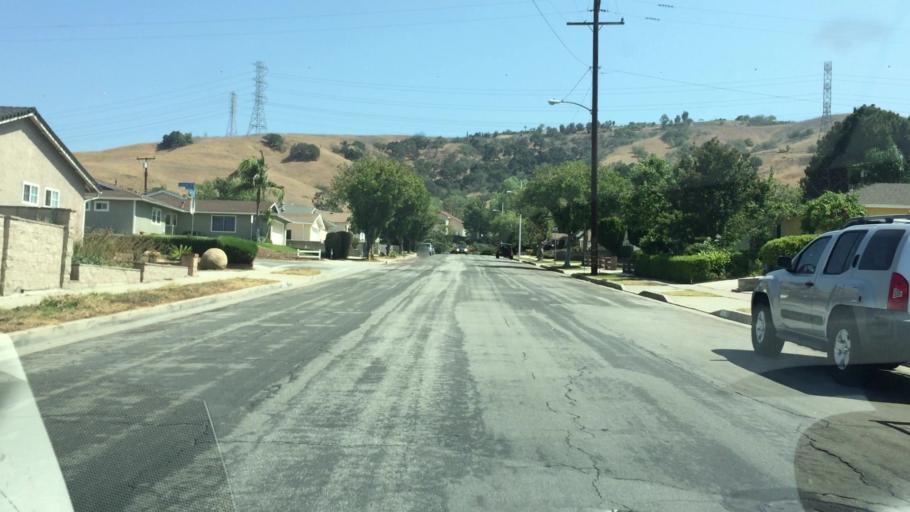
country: US
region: California
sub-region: Los Angeles County
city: Rowland Heights
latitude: 33.9710
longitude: -117.9023
